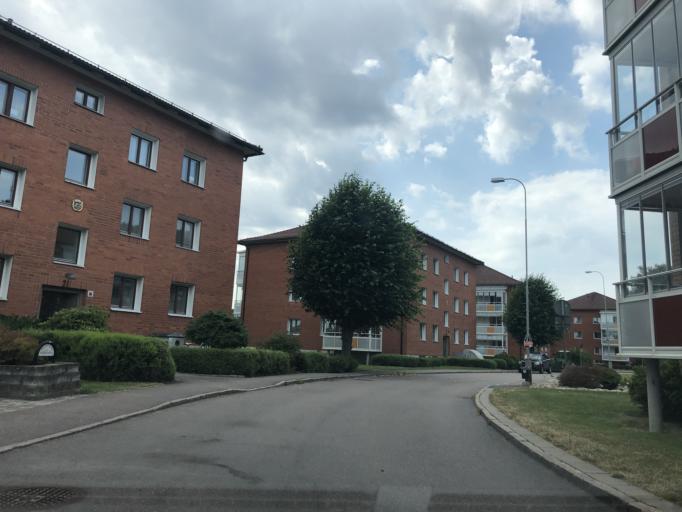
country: SE
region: Vaestra Goetaland
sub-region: Goteborg
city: Majorna
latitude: 57.7317
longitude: 11.9259
